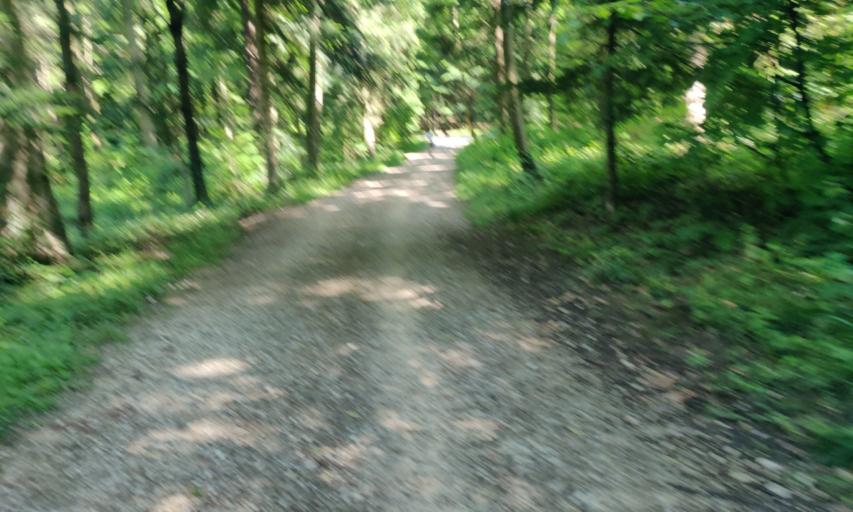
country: CH
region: Basel-Landschaft
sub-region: Bezirk Arlesheim
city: Pfeffingen
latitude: 47.4684
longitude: 7.5751
